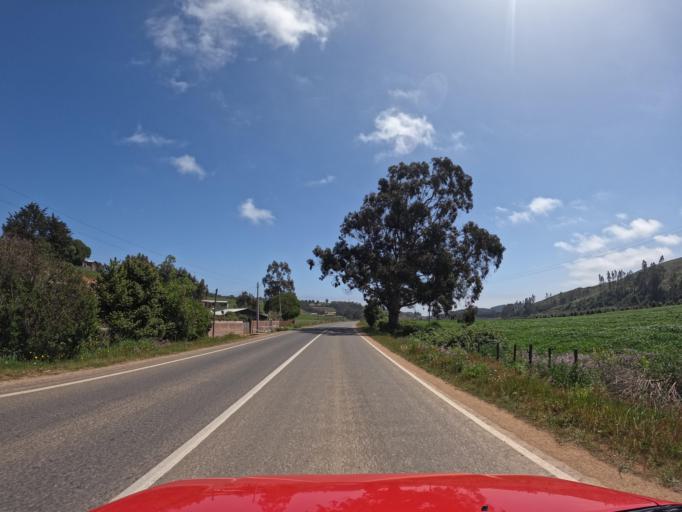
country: CL
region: O'Higgins
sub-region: Provincia de Colchagua
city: Santa Cruz
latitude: -34.6516
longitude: -72.0255
